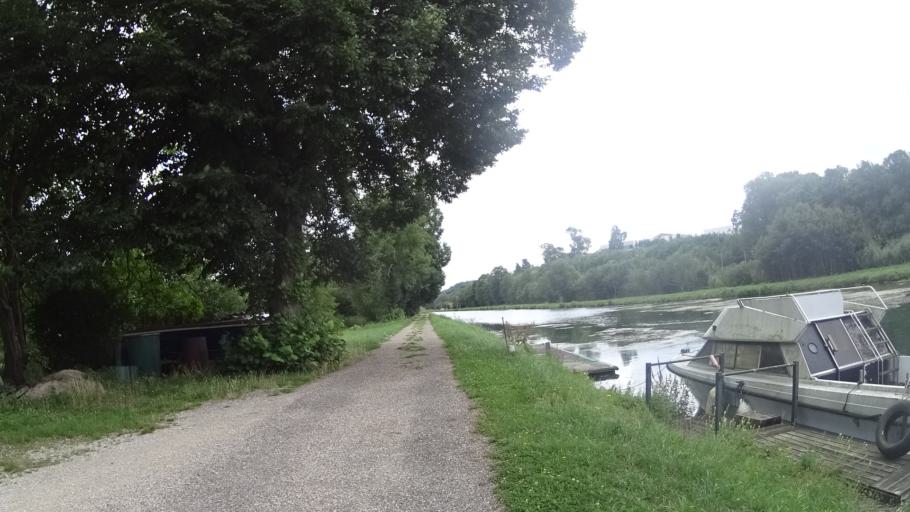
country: FR
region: Lorraine
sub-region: Departement de la Meuse
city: Commercy
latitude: 48.7610
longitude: 5.6002
